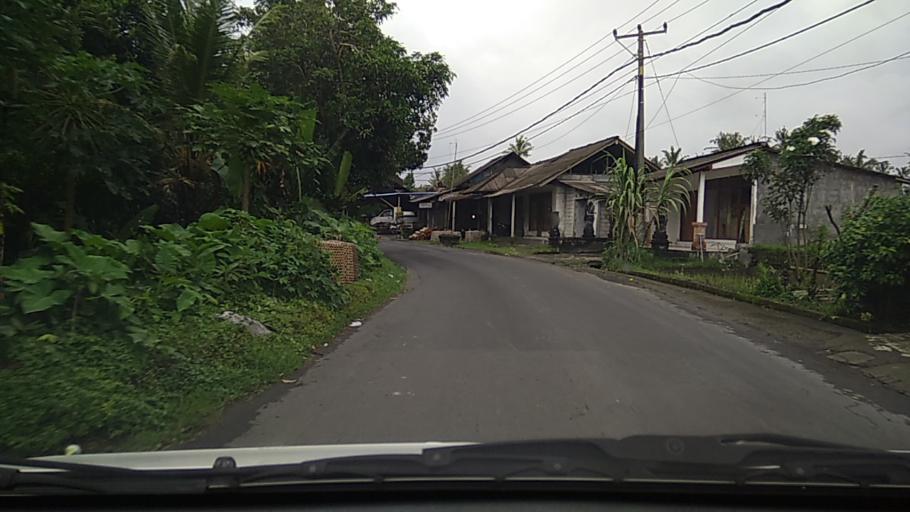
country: ID
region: Bali
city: Banjar Manukayaanyar
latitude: -8.4162
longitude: 115.2977
